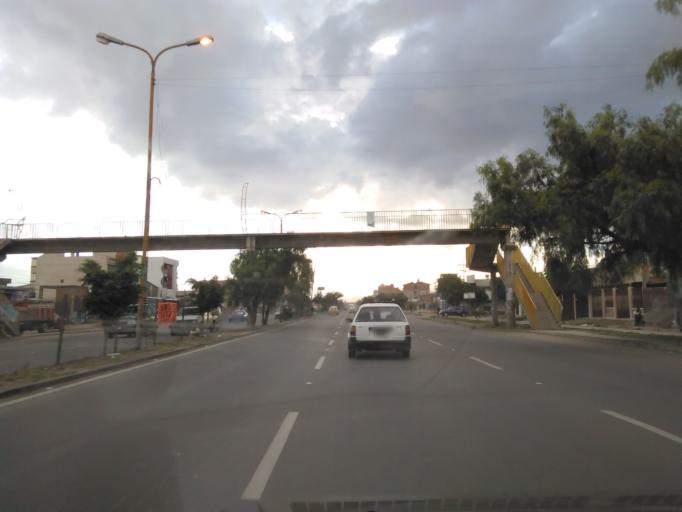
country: BO
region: Cochabamba
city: Cochabamba
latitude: -17.3920
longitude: -66.2145
